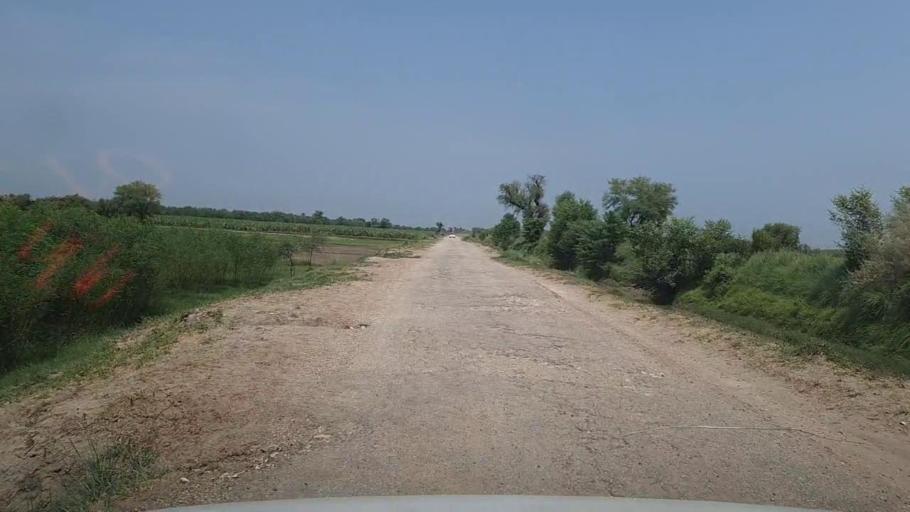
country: PK
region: Sindh
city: Karaundi
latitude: 26.8796
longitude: 68.3353
